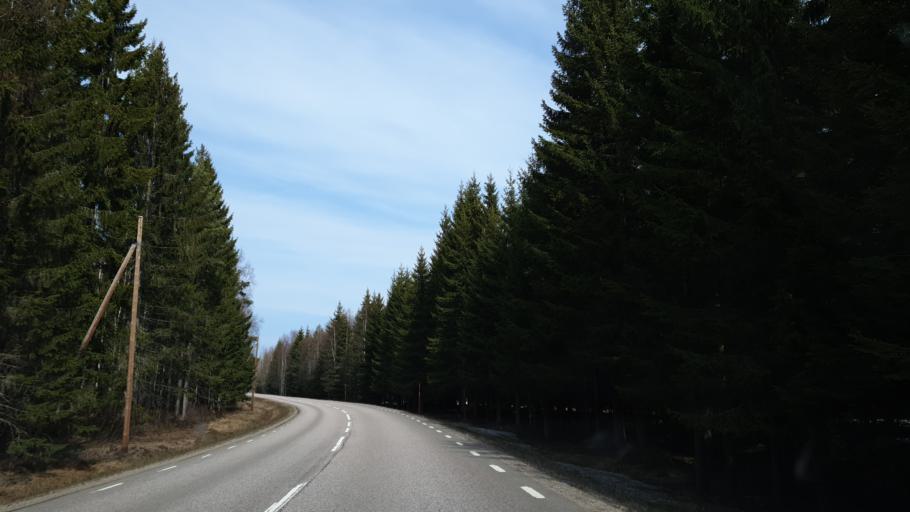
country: SE
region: Gaevleborg
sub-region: Gavle Kommun
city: Norrsundet
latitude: 60.9690
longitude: 17.0514
